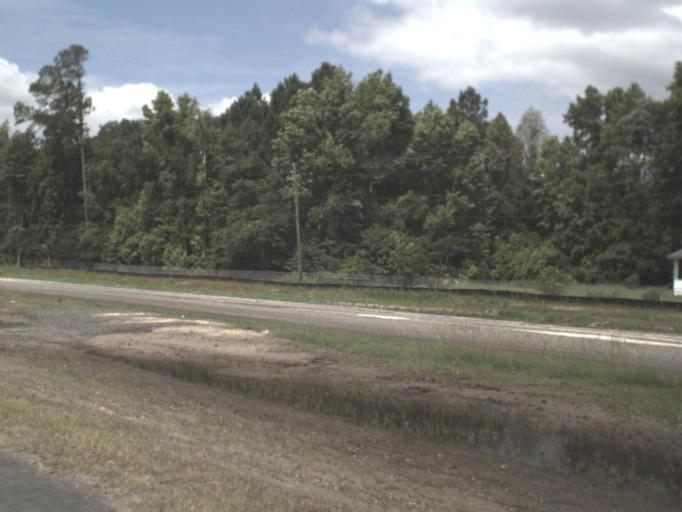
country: US
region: Florida
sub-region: Nassau County
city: Callahan
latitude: 30.5494
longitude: -81.8445
